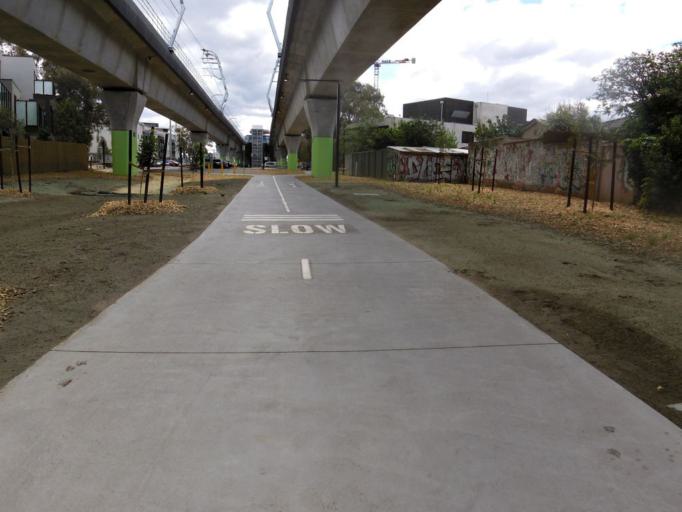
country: AU
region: Victoria
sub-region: Glen Eira
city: Carnegie
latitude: -37.8874
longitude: 145.0612
